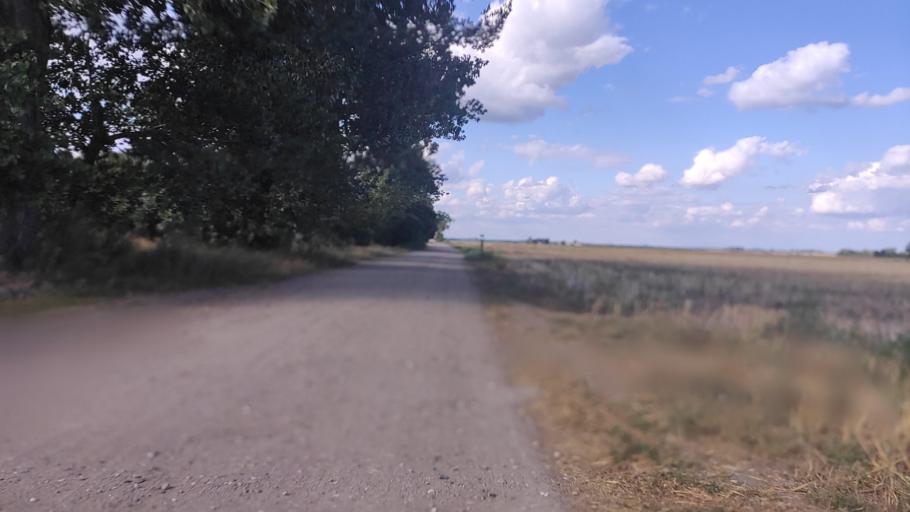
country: PL
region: Greater Poland Voivodeship
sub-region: Powiat poznanski
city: Swarzedz
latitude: 52.4156
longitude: 17.1408
